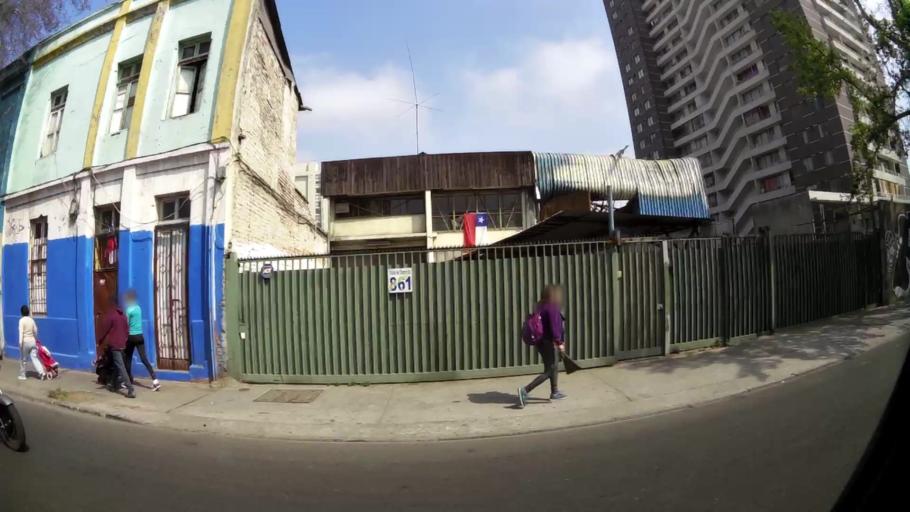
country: CL
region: Santiago Metropolitan
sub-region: Provincia de Santiago
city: Santiago
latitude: -33.4553
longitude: -70.6437
